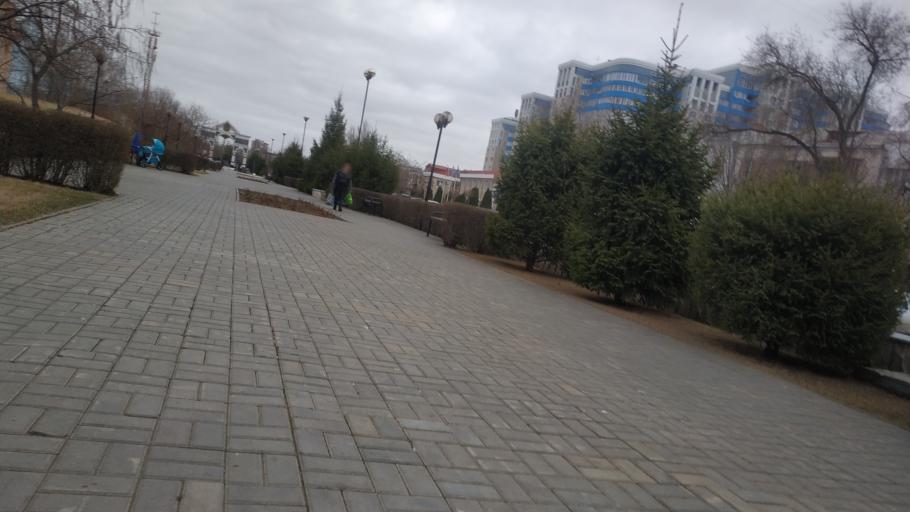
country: RU
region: Astrakhan
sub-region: Gorod Astrakhan'
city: Astrakhan'
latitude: 46.3462
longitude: 48.0179
